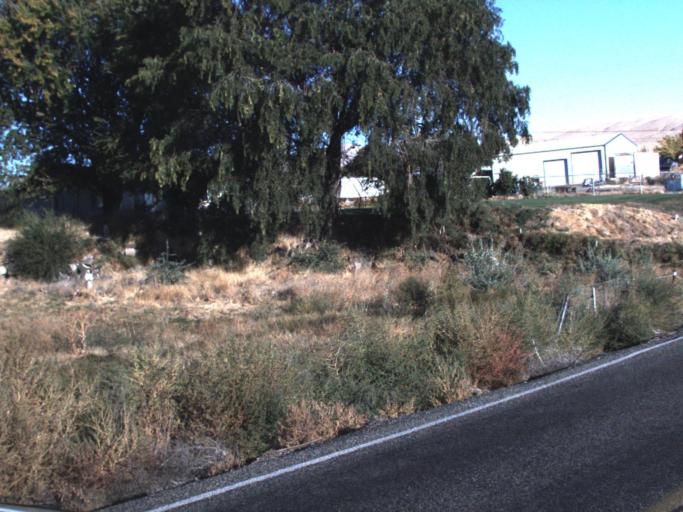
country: US
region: Washington
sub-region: Benton County
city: Benton City
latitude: 46.2970
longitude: -119.4937
